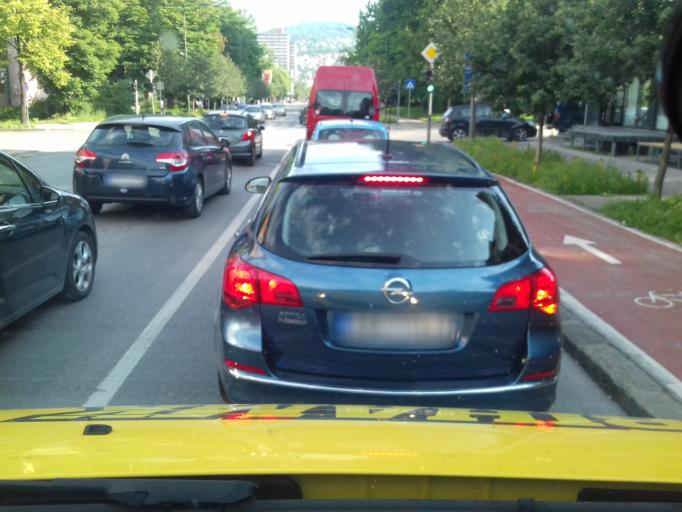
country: BA
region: Federation of Bosnia and Herzegovina
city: Kobilja Glava
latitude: 43.8506
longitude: 18.3938
